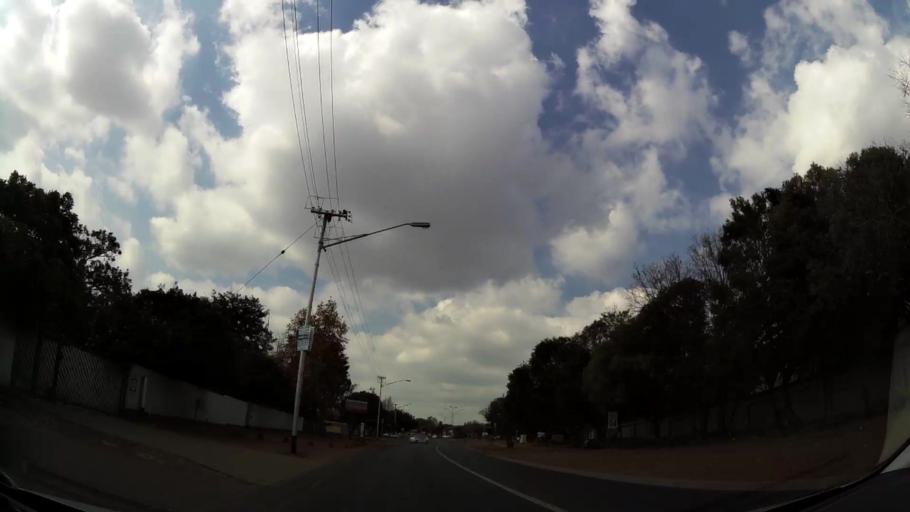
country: ZA
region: Gauteng
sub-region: City of Tshwane Metropolitan Municipality
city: Pretoria
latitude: -25.7778
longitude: 28.2873
